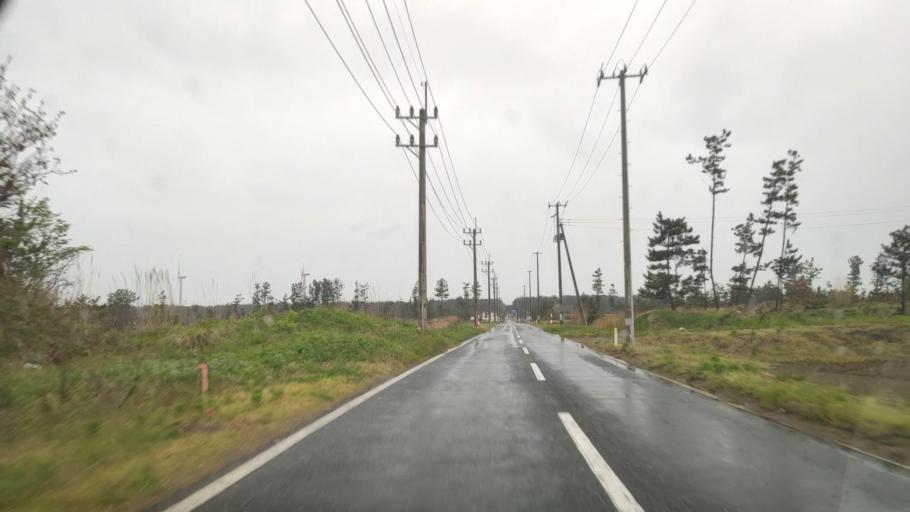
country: JP
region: Akita
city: Noshiromachi
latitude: 40.0960
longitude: 139.9721
